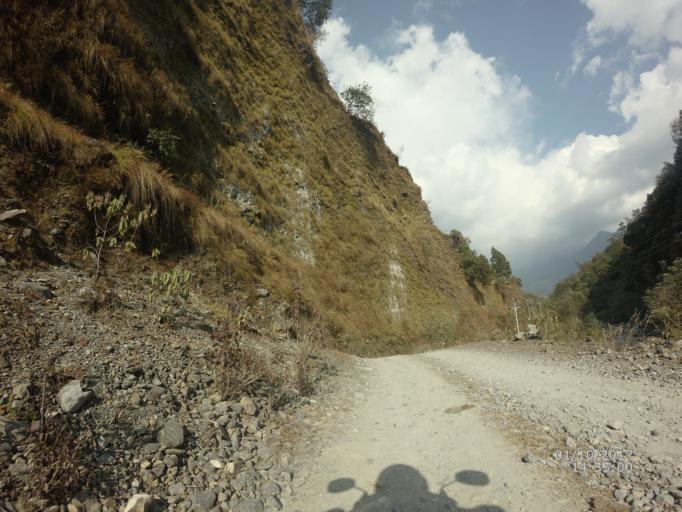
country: NP
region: Western Region
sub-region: Gandaki Zone
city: Pokhara
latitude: 28.3416
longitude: 83.9644
